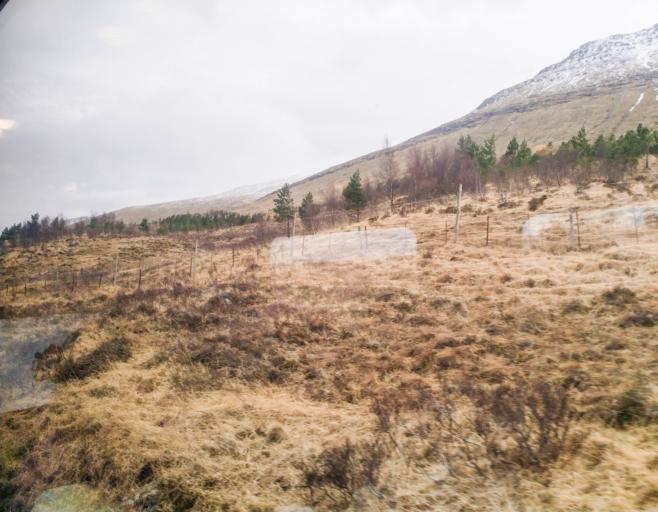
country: GB
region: Scotland
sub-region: Highland
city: Spean Bridge
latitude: 56.5615
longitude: -4.7131
